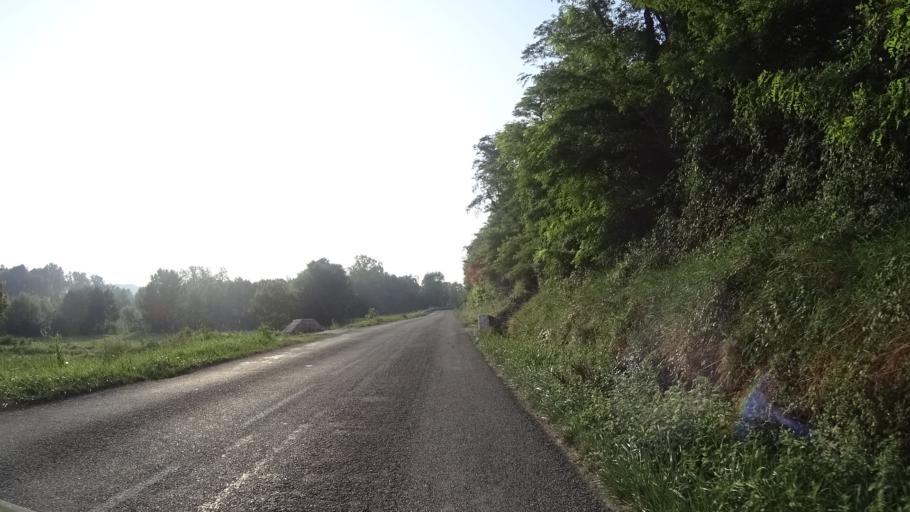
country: FR
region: Midi-Pyrenees
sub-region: Departement de l'Ariege
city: Mirepoix
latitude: 43.0854
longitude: 1.9235
